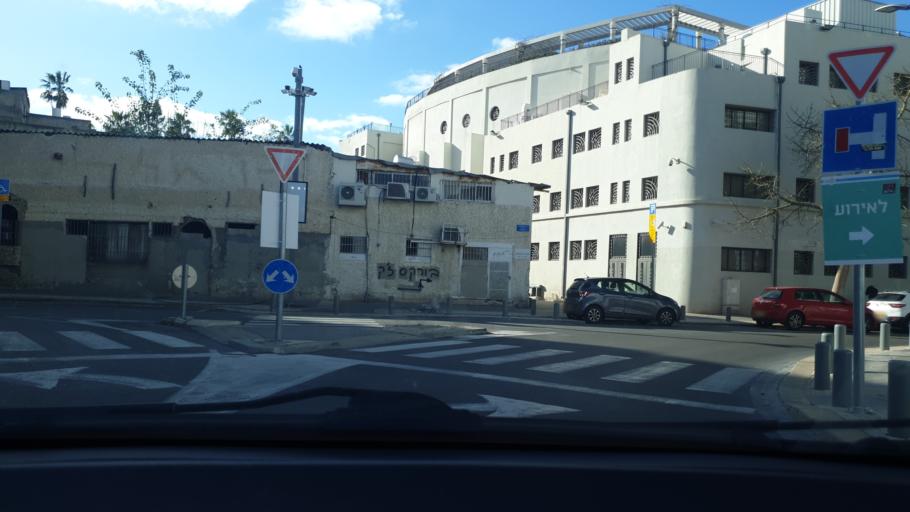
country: IL
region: Tel Aviv
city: Yafo
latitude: 32.0515
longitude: 34.7600
